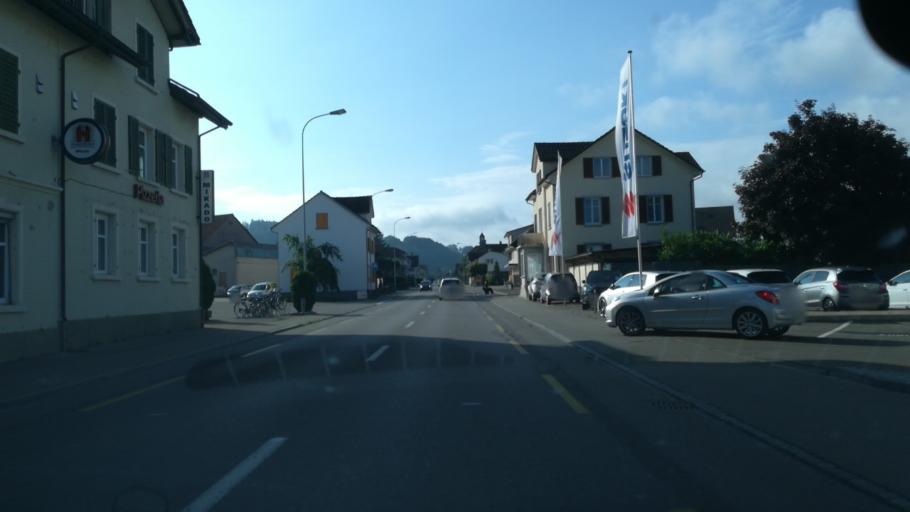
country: CH
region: Thurgau
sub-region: Weinfelden District
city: Sulgen
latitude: 47.5278
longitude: 9.1957
